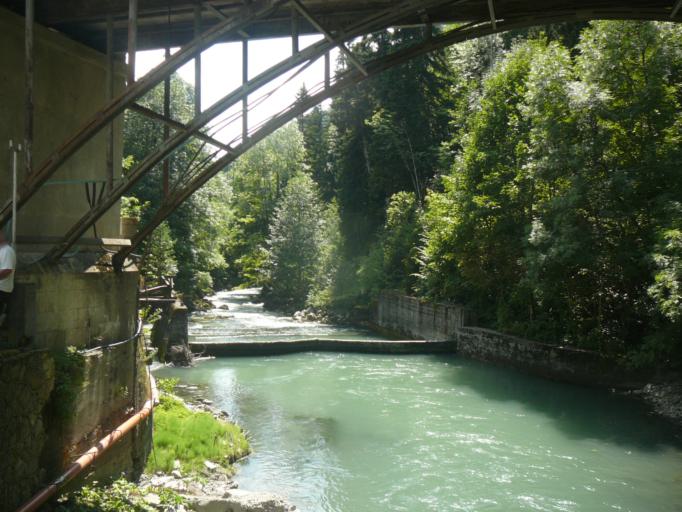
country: GE
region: Abkhazia
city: Gagra
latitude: 43.4716
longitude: 40.5331
